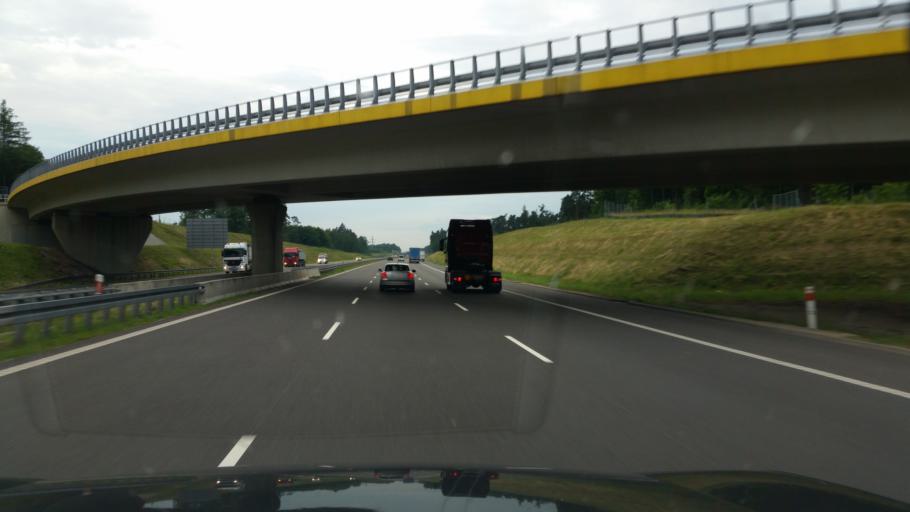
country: PL
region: Silesian Voivodeship
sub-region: Powiat rybnicki
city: Stanowice
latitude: 50.1188
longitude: 18.6838
